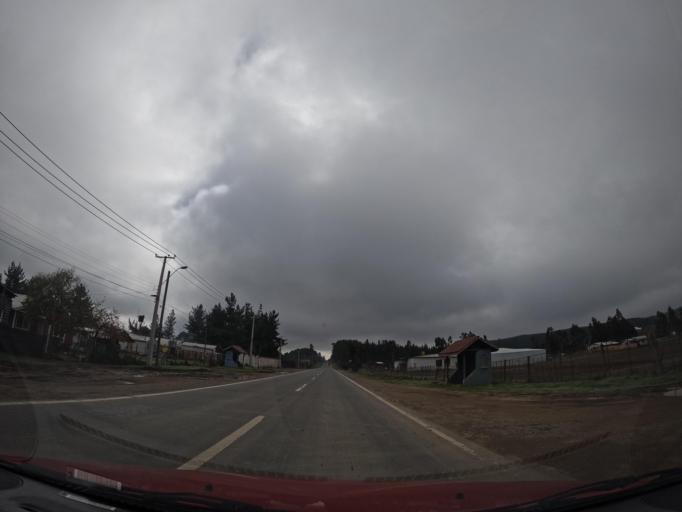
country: CL
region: Maule
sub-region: Provincia de Cauquenes
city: Cauquenes
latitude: -36.2613
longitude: -72.5481
